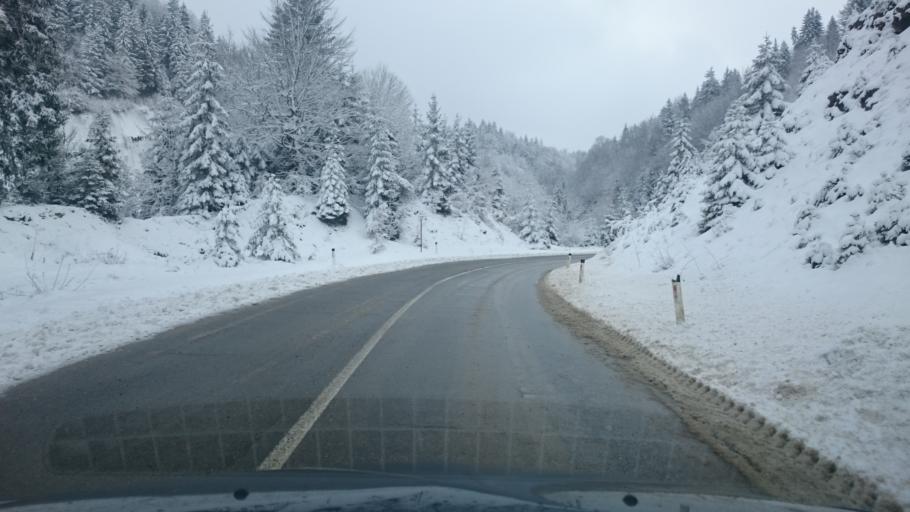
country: BA
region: Republika Srpska
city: Skender Vakuf
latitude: 44.4714
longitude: 17.3865
